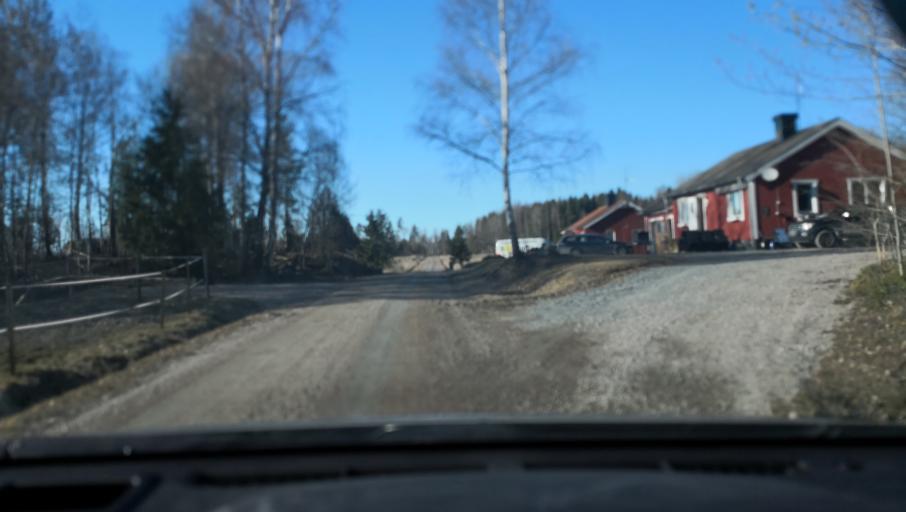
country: SE
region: Dalarna
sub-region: Avesta Kommun
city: Horndal
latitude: 60.1717
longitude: 16.6333
